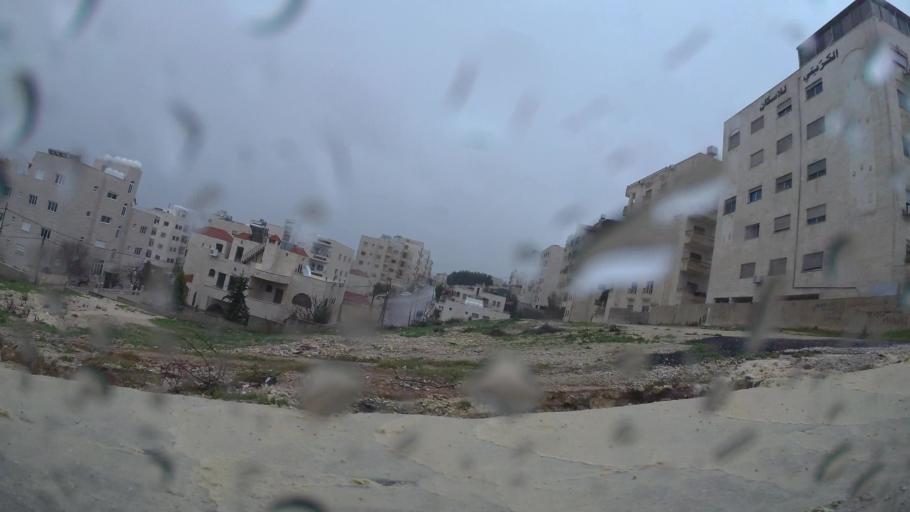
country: JO
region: Amman
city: Al Jubayhah
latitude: 32.0228
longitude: 35.8895
